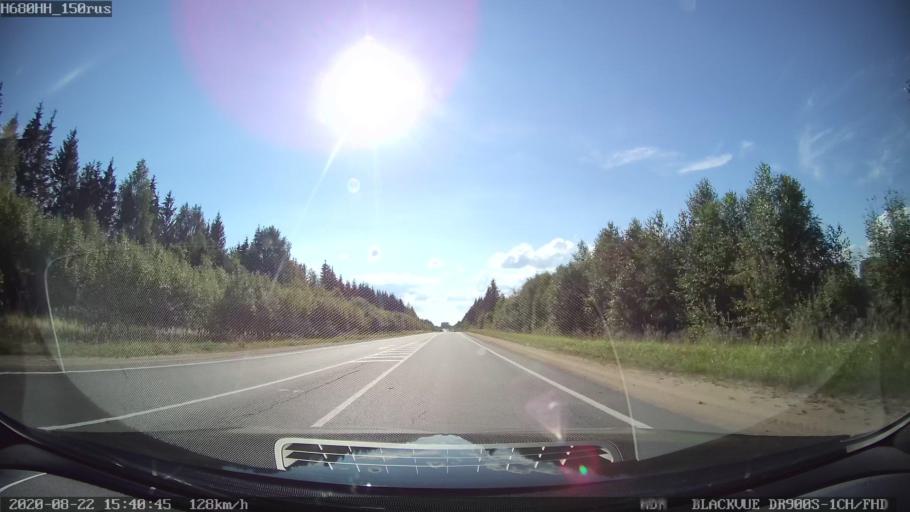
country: RU
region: Tverskaya
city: Bezhetsk
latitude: 57.7532
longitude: 36.5870
